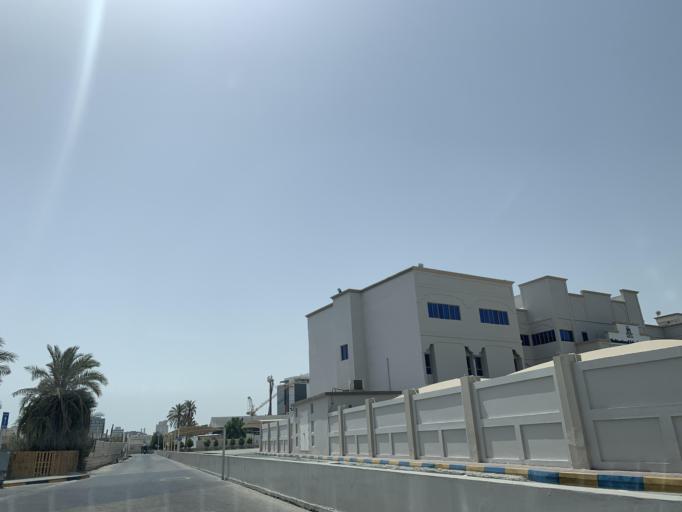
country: BH
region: Manama
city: Manama
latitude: 26.2127
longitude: 50.5933
